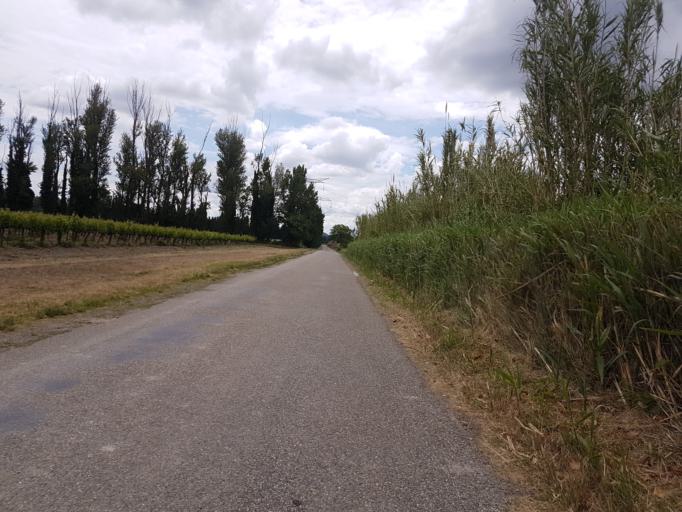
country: FR
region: Languedoc-Roussillon
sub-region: Departement du Gard
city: Vallabregues
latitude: 43.8785
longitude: 4.6278
